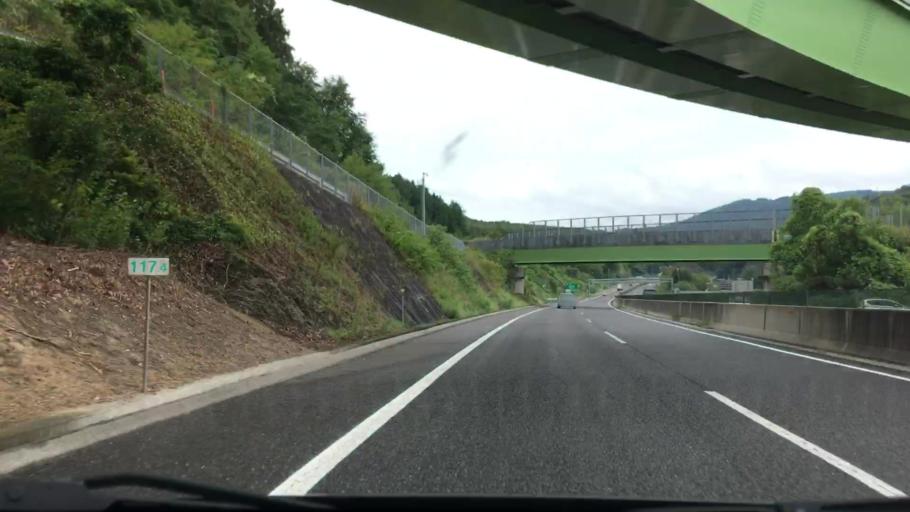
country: JP
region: Hyogo
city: Yamazakicho-nakabirose
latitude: 35.0216
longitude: 134.3901
